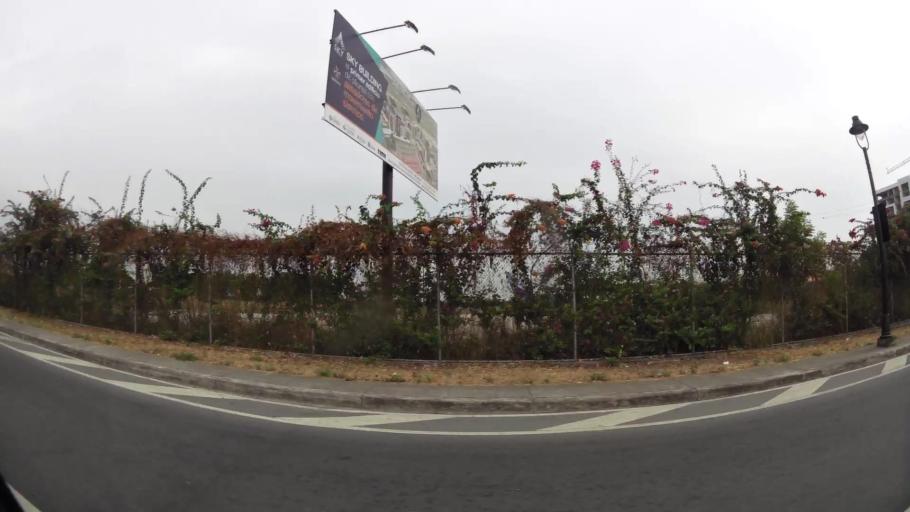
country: EC
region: Guayas
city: Eloy Alfaro
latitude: -2.1461
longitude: -79.8813
